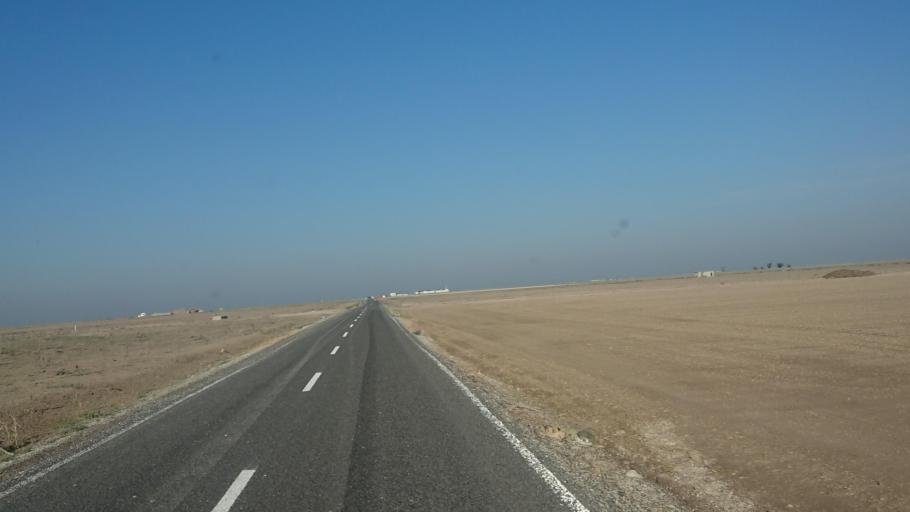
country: TR
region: Aksaray
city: Yesilova
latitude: 38.3879
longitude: 33.7599
